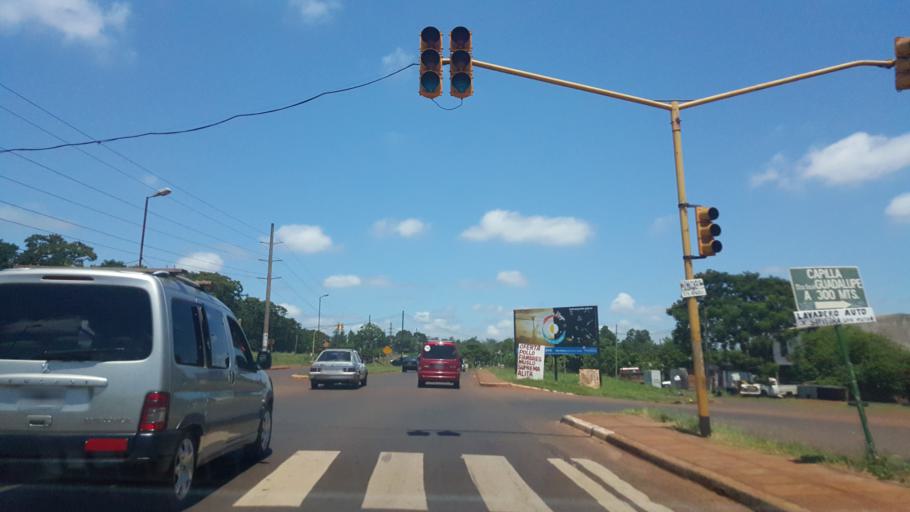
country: AR
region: Misiones
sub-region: Departamento de Capital
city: Posadas
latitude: -27.4212
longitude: -55.9319
